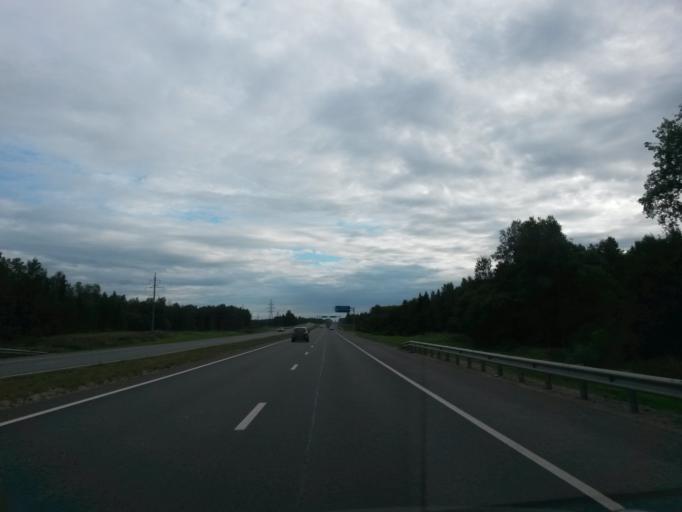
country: RU
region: Jaroslavl
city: Krasnyye Tkachi
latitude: 57.3994
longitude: 39.6470
